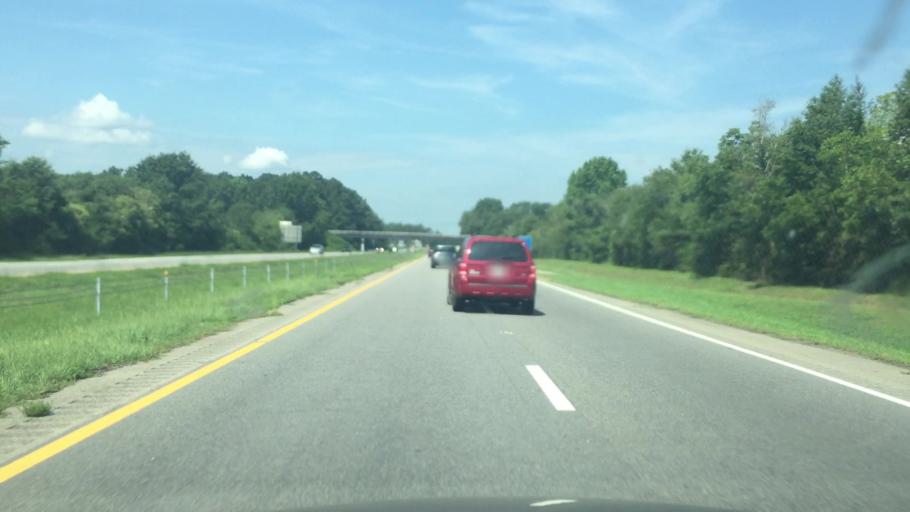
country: US
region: North Carolina
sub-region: Scotland County
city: Laurinburg
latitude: 34.7548
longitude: -79.4612
